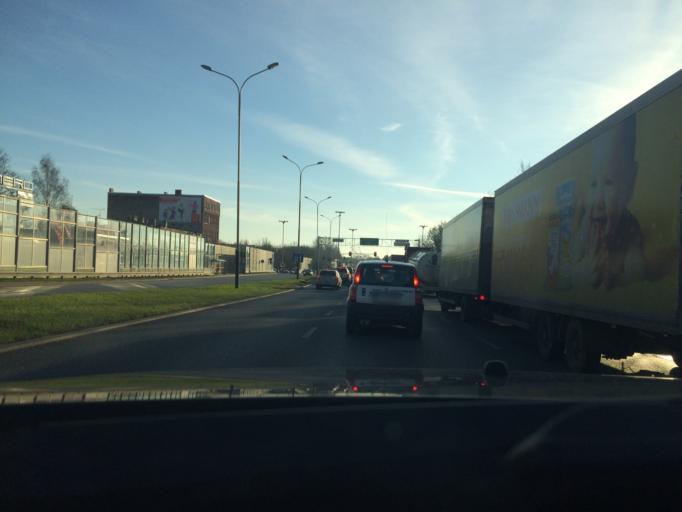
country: PL
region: Lodz Voivodeship
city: Lodz
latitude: 51.7383
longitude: 19.4422
